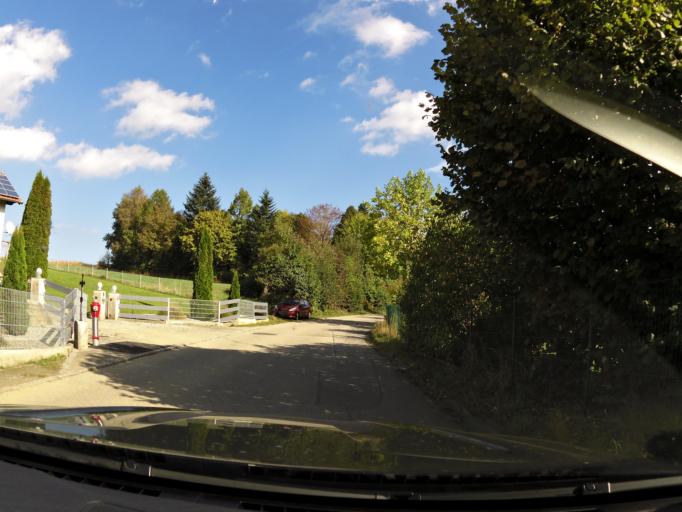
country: DE
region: Bavaria
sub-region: Lower Bavaria
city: Vilsheim
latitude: 48.4292
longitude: 12.1301
